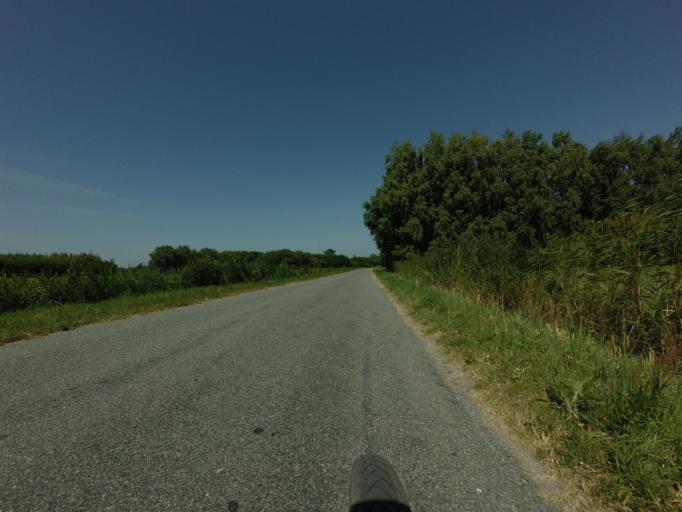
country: DK
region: North Denmark
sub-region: Laeso Kommune
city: Byrum
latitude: 57.2533
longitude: 10.9888
